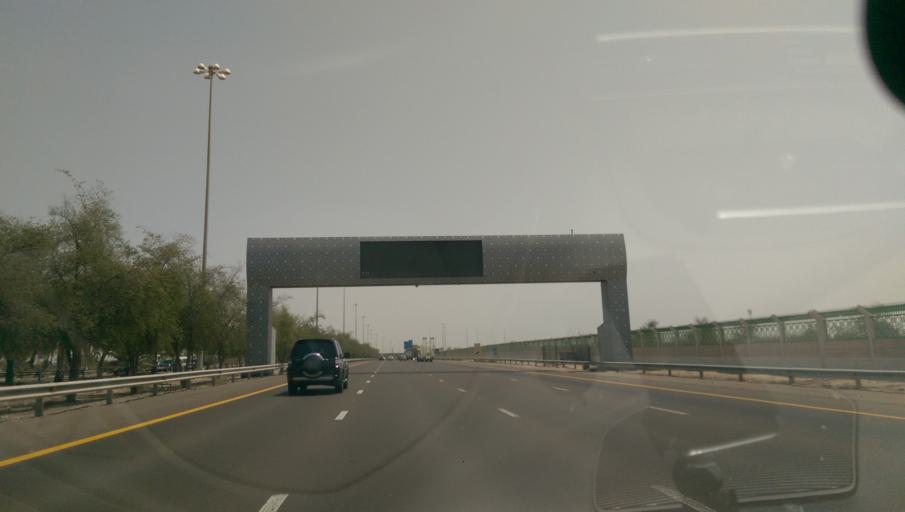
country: AE
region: Abu Dhabi
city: Abu Dhabi
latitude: 24.6141
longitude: 54.7142
